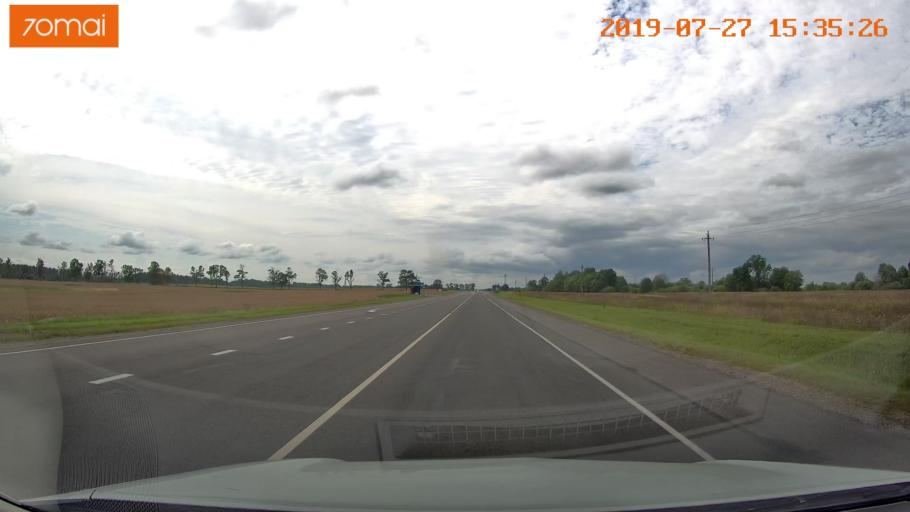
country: RU
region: Kaliningrad
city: Nesterov
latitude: 54.6136
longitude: 22.3970
